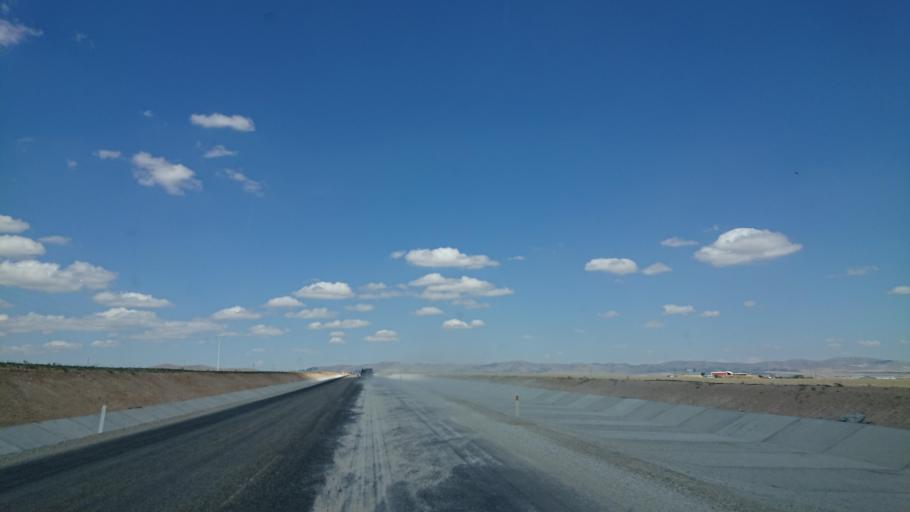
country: TR
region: Kirsehir
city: Kirsehir
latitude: 39.1278
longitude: 34.0350
